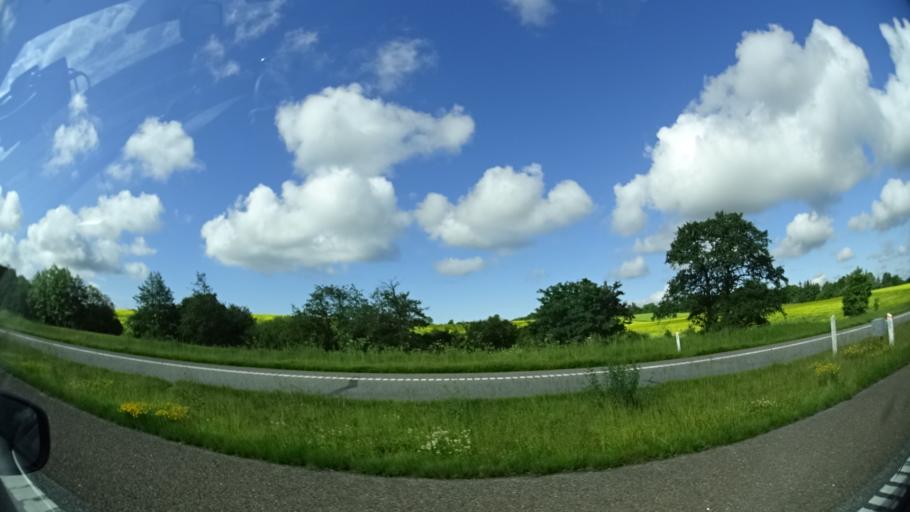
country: DK
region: Central Jutland
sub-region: Syddjurs Kommune
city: Ronde
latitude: 56.3012
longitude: 10.5091
